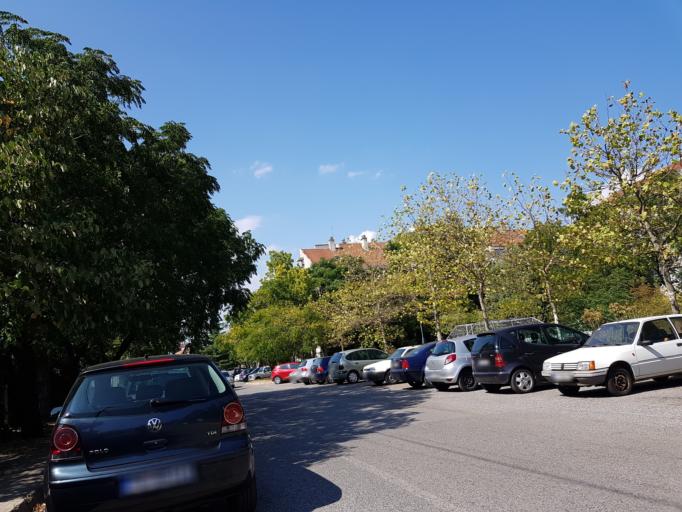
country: ME
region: Podgorica
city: Podgorica
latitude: 42.4316
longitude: 19.2781
